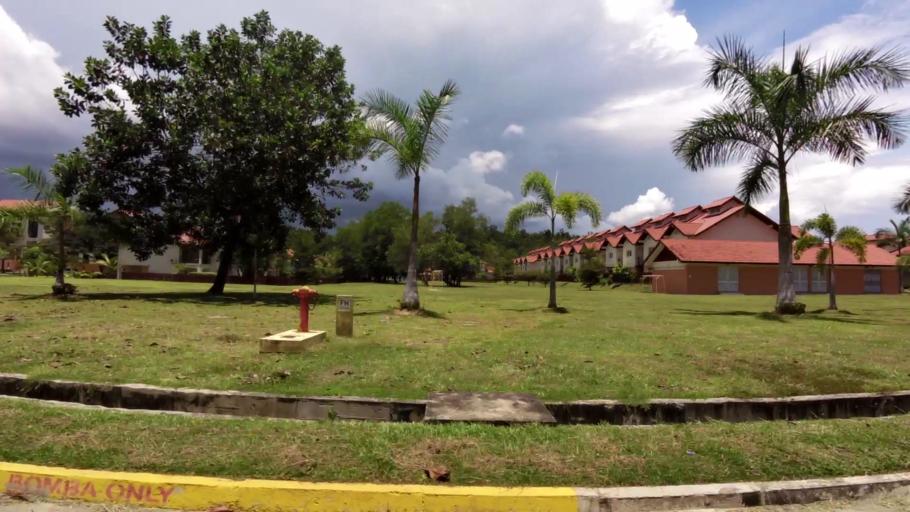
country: BN
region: Brunei and Muara
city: Bandar Seri Begawan
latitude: 4.9549
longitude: 114.8926
